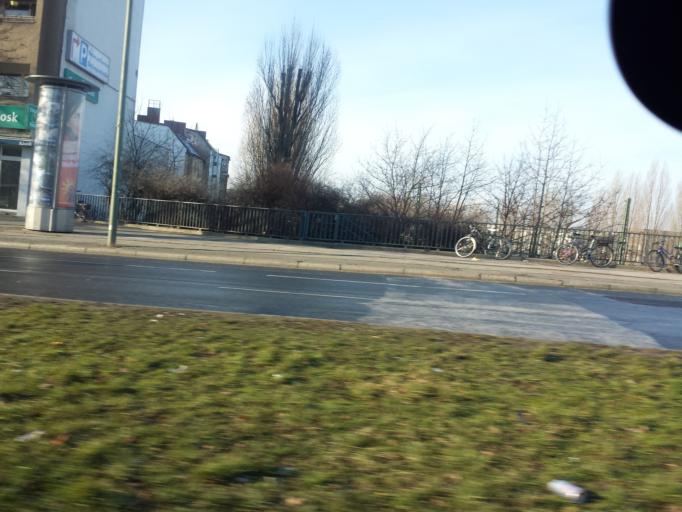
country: DE
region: Berlin
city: Moabit
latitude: 52.5338
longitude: 13.3284
